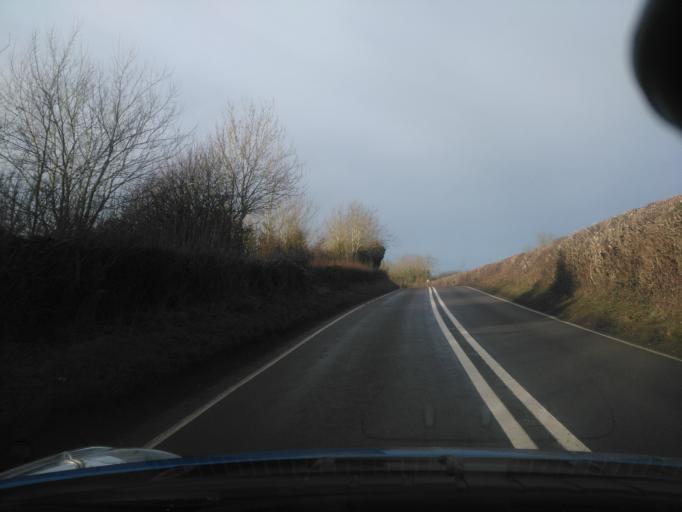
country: GB
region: England
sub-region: Oxfordshire
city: Chipping Norton
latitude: 51.9532
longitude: -1.5942
